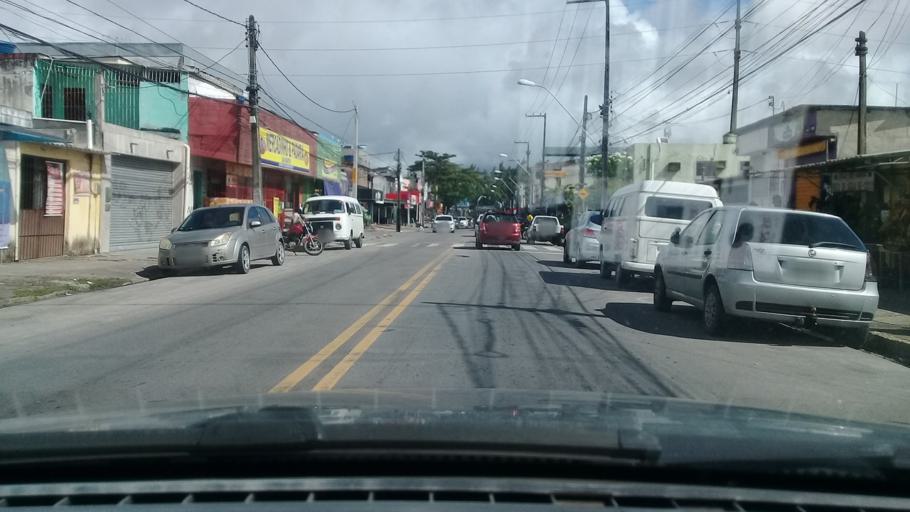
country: BR
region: Pernambuco
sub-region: Recife
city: Recife
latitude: -8.0687
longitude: -34.9282
